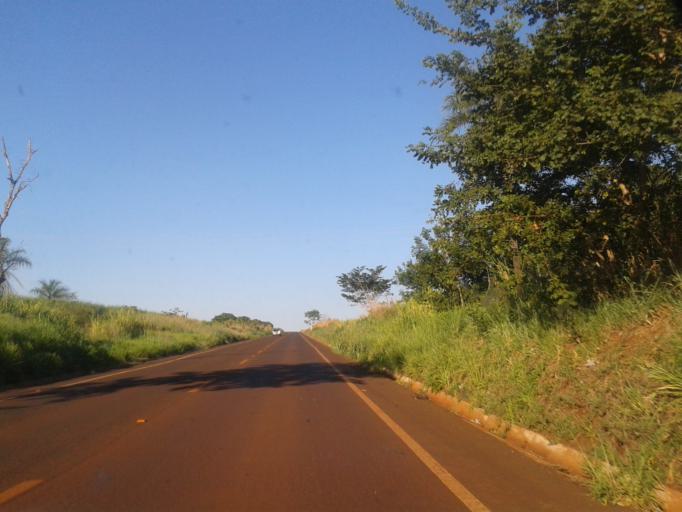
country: BR
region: Minas Gerais
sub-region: Capinopolis
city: Capinopolis
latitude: -18.7075
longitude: -49.7004
